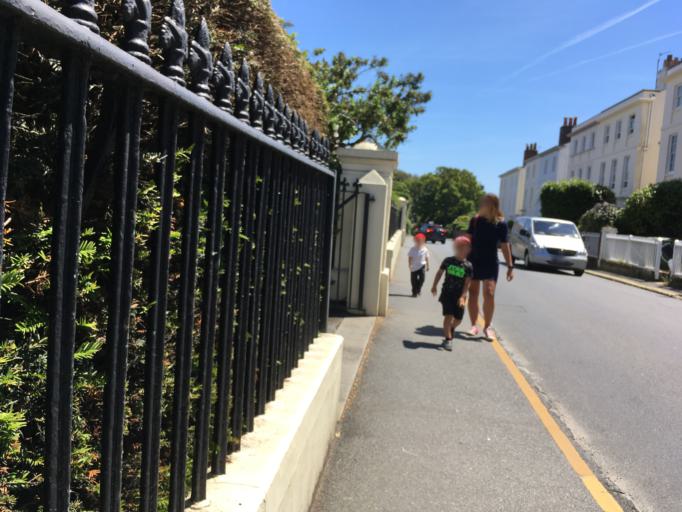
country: GG
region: St Peter Port
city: Saint Peter Port
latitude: 49.4595
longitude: -2.5434
